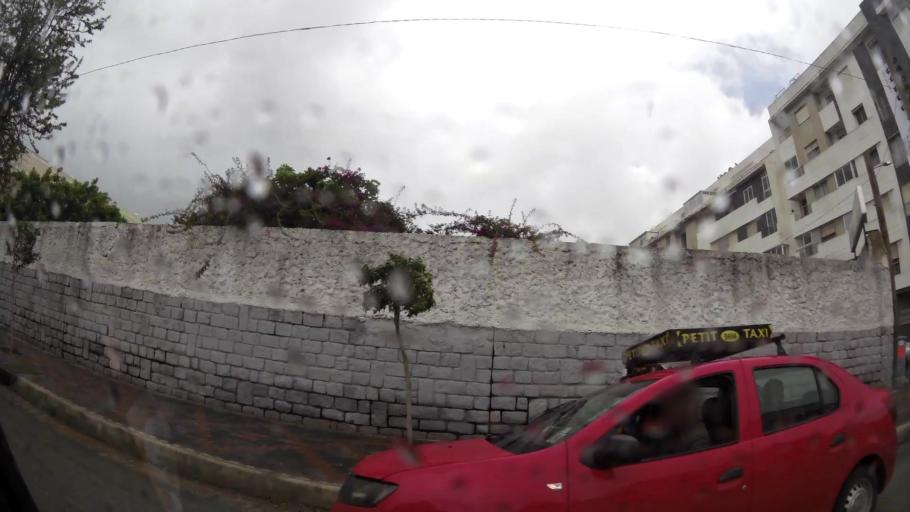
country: MA
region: Grand Casablanca
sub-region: Casablanca
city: Casablanca
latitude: 33.5808
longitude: -7.5973
